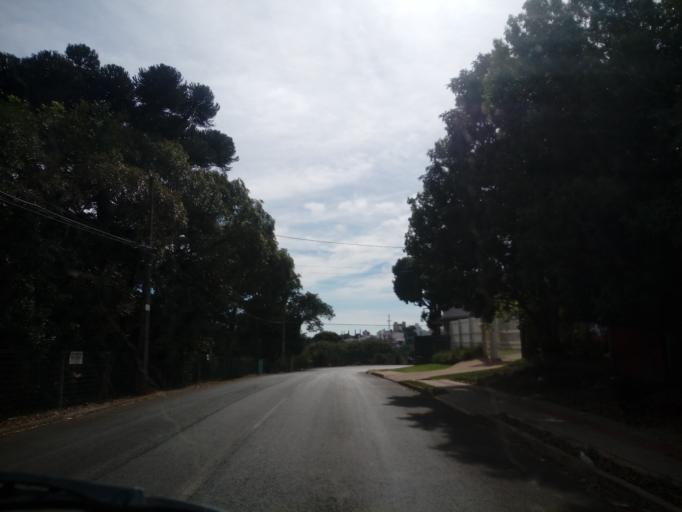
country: BR
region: Santa Catarina
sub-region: Chapeco
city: Chapeco
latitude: -27.1215
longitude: -52.6146
